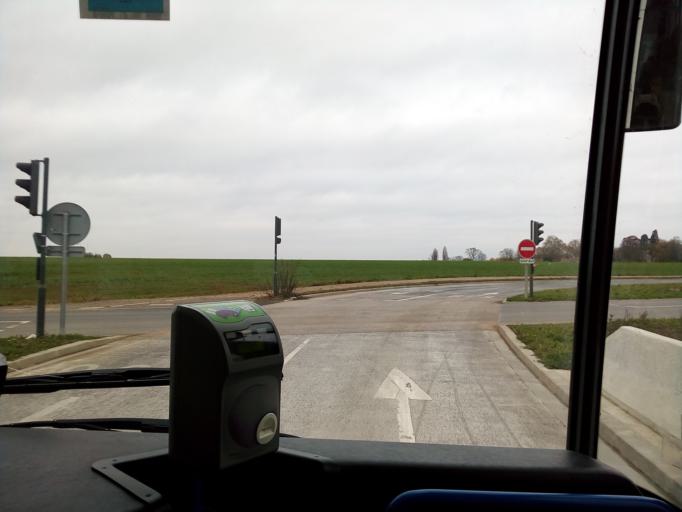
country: FR
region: Ile-de-France
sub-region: Departement de l'Essonne
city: Bures-sur-Yvette
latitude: 48.7153
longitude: 2.1778
